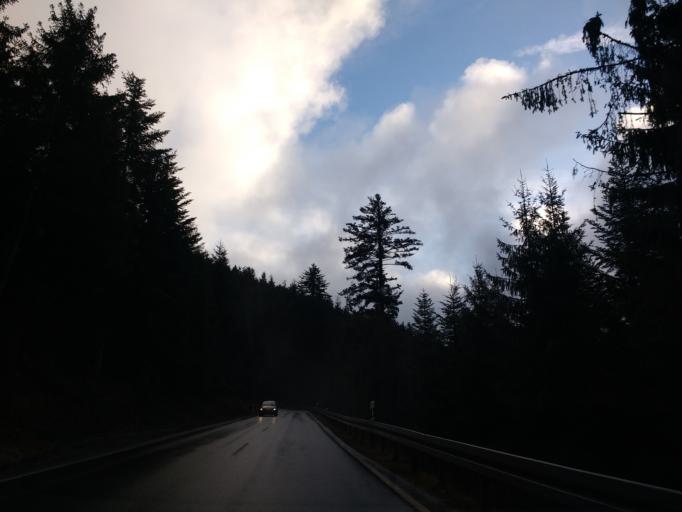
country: DE
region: Baden-Wuerttemberg
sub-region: Freiburg Region
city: Seebach
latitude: 48.5800
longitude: 8.2141
